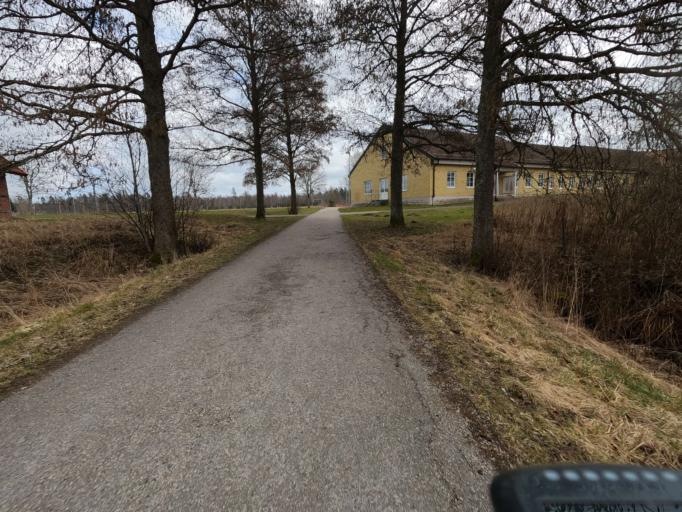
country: SE
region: Joenkoeping
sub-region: Varnamo Kommun
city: Rydaholm
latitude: 56.8618
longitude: 14.1718
